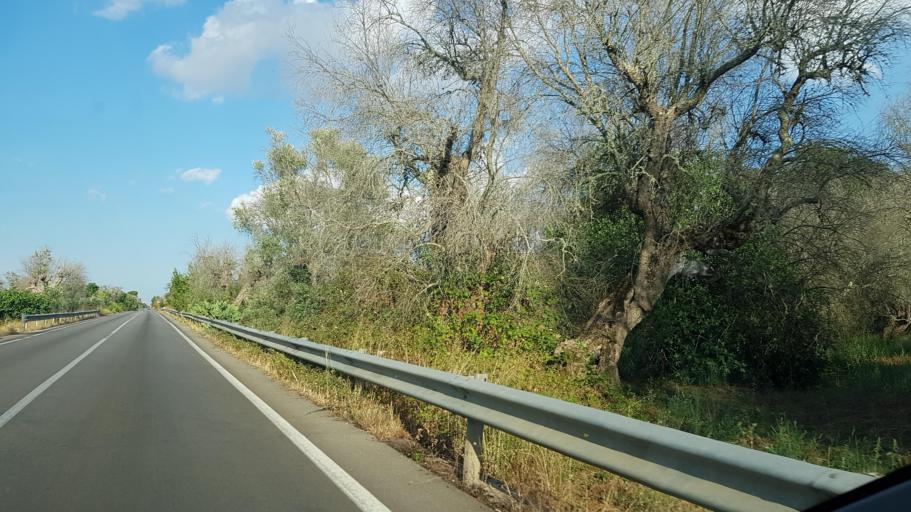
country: IT
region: Apulia
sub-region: Provincia di Lecce
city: Miggiano
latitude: 39.9639
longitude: 18.2902
